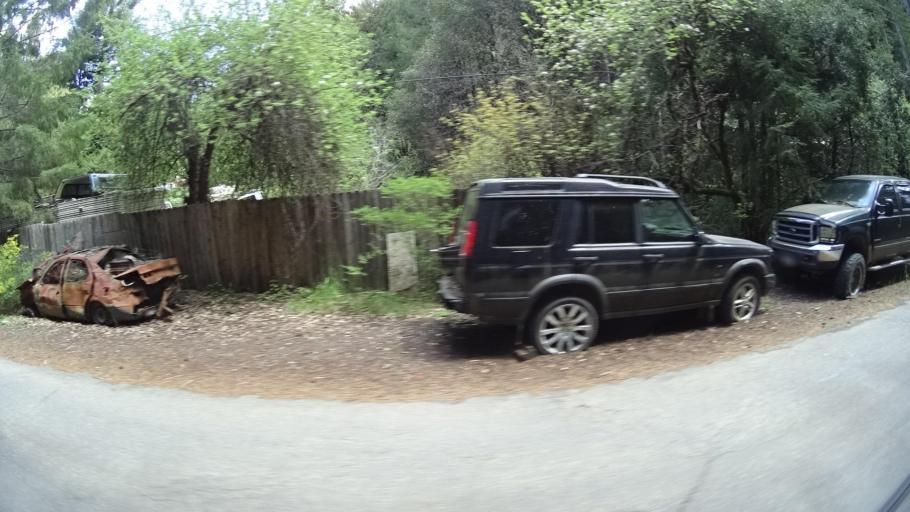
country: US
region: California
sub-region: Humboldt County
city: Redway
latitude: 40.0217
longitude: -123.9382
